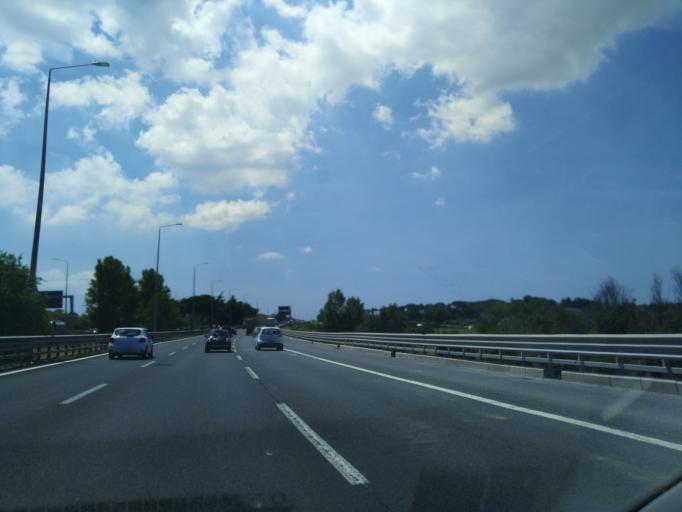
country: IT
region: Latium
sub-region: Citta metropolitana di Roma Capitale
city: Borgo Lotti
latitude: 41.8018
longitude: 12.5523
